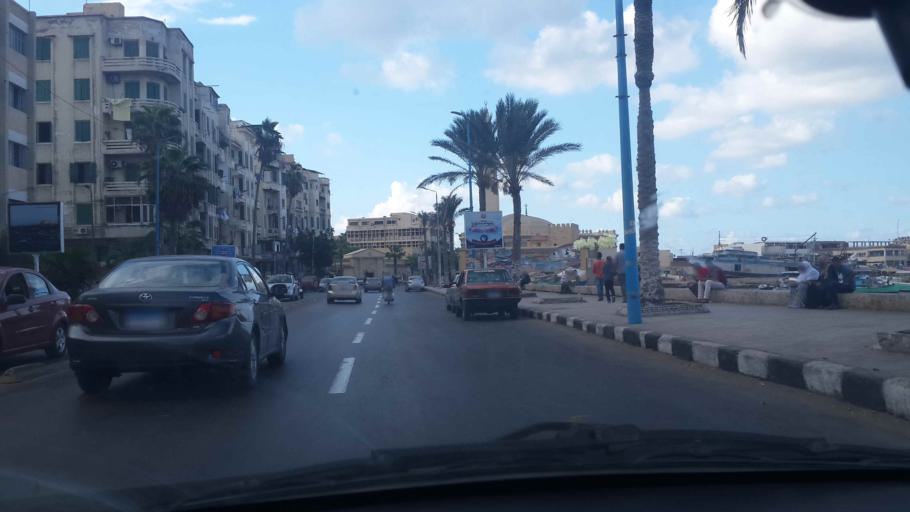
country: EG
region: Alexandria
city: Alexandria
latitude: 31.2086
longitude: 29.8828
